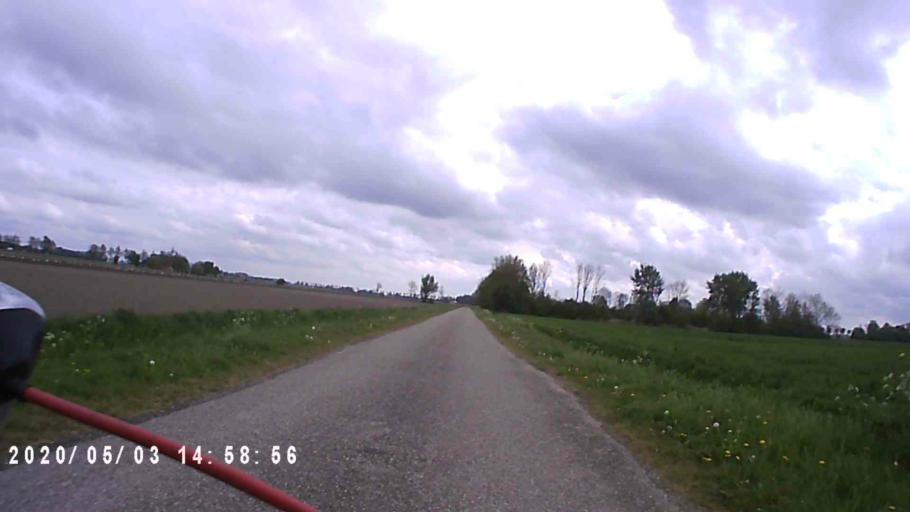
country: NL
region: Groningen
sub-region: Gemeente Zuidhorn
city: Oldehove
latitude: 53.3606
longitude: 6.4390
